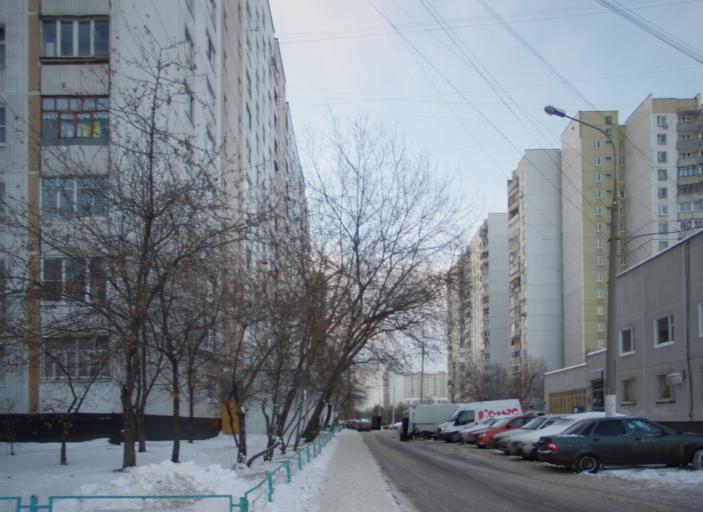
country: RU
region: Moscow
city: Tsaritsyno
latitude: 55.6401
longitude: 37.6651
